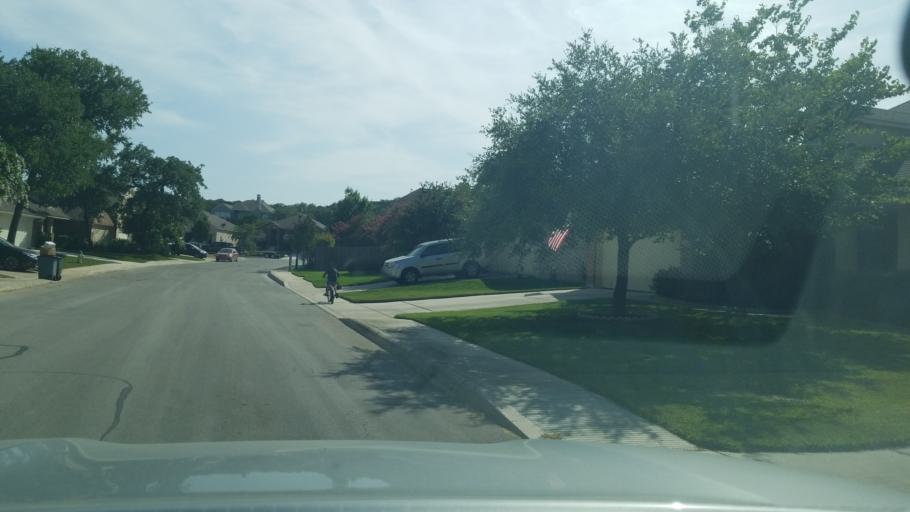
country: US
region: Texas
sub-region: Bexar County
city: Timberwood Park
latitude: 29.6875
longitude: -98.4746
